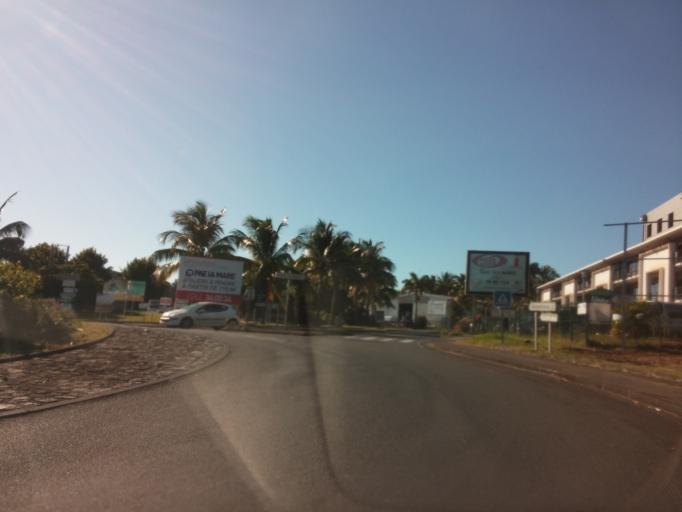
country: RE
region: Reunion
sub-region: Reunion
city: Sainte-Marie
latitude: -20.8996
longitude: 55.5269
